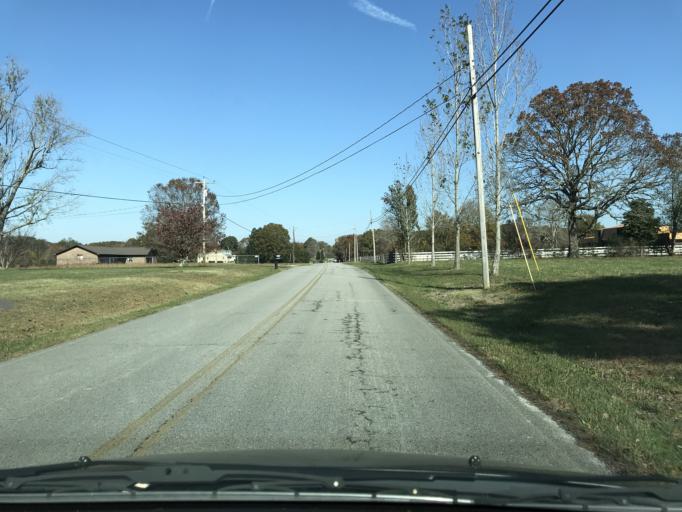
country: US
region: Tennessee
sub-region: Coffee County
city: Tullahoma
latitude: 35.3923
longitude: -86.1639
